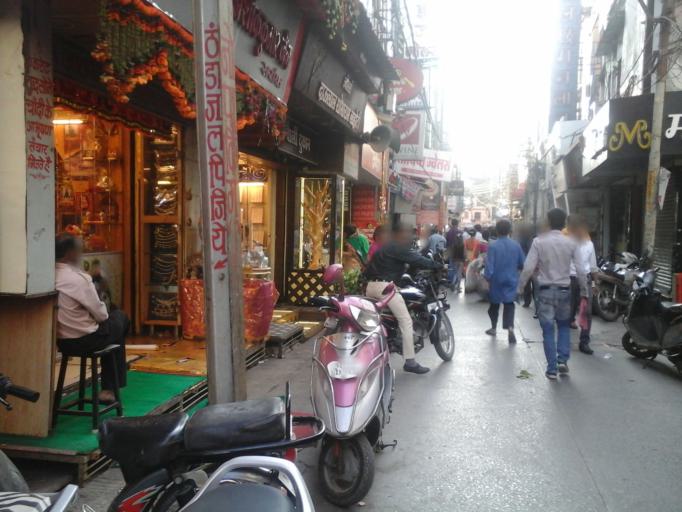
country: IN
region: Madhya Pradesh
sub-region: Indore
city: Indore
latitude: 22.7189
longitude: 75.8528
